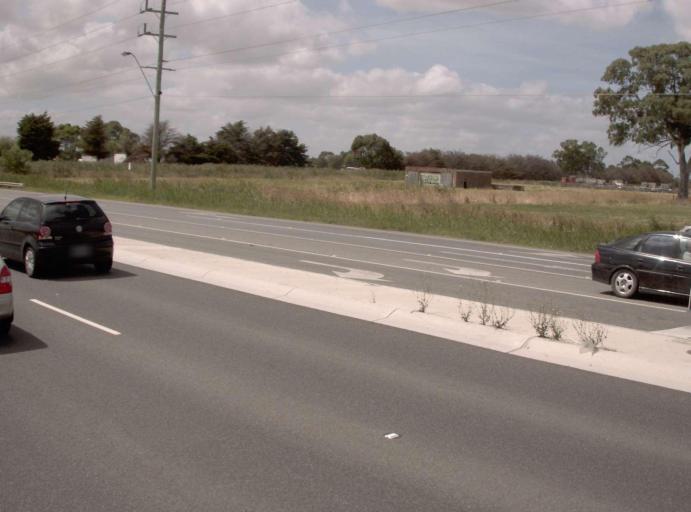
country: AU
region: Victoria
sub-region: Casey
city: Cranbourne West
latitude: -38.0790
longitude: 145.2515
